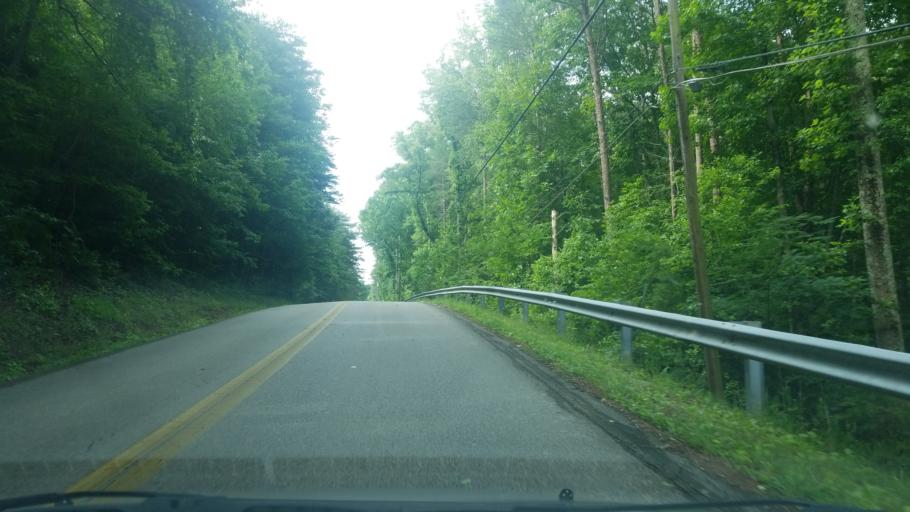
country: US
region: Tennessee
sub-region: Hamilton County
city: Collegedale
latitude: 35.0212
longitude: -85.0604
